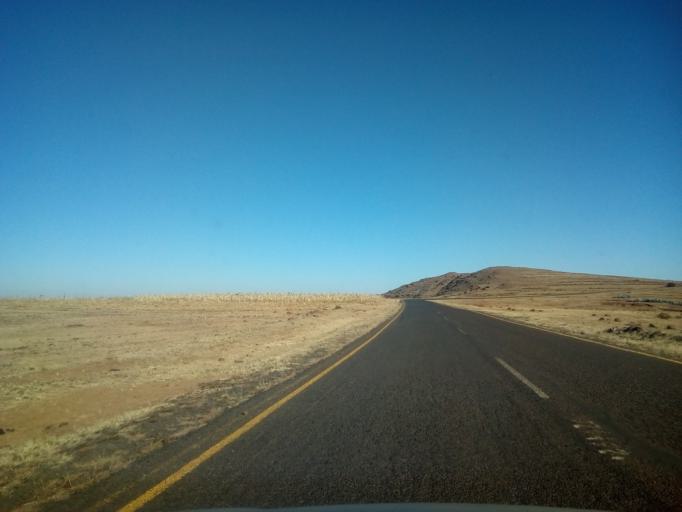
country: LS
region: Berea
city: Teyateyaneng
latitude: -29.2542
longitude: 27.7773
